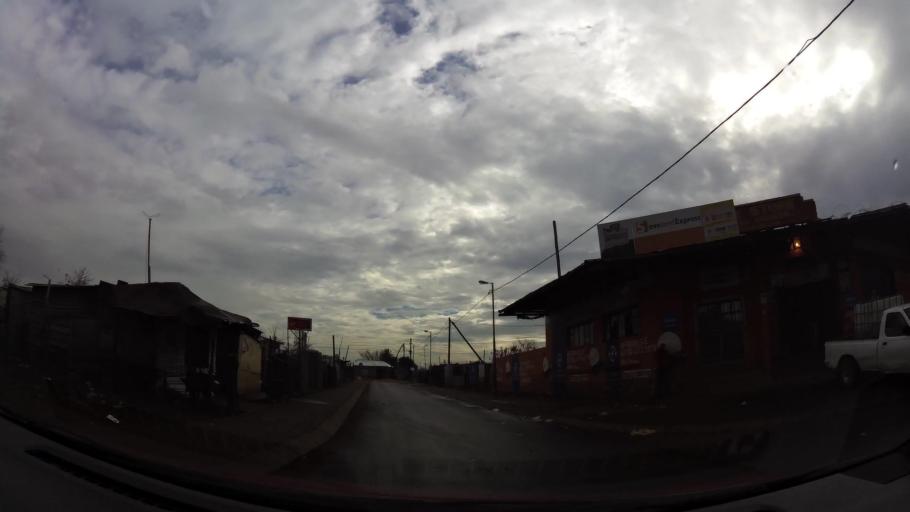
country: ZA
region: Gauteng
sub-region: City of Johannesburg Metropolitan Municipality
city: Soweto
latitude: -26.2856
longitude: 27.8417
